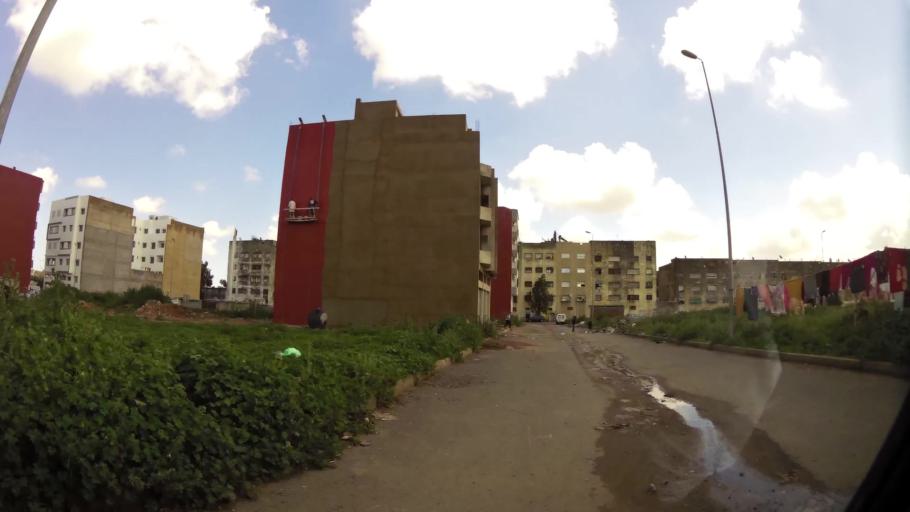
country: MA
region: Grand Casablanca
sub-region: Casablanca
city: Casablanca
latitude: 33.5383
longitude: -7.5580
